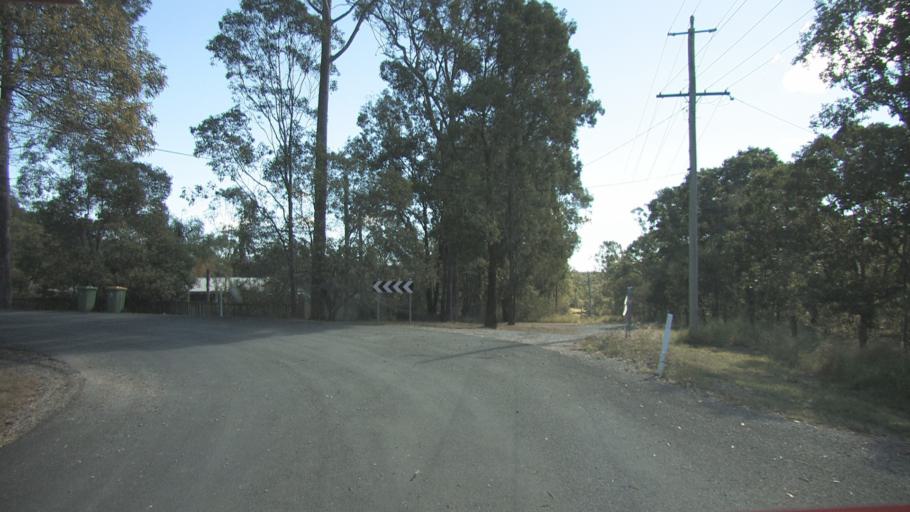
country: AU
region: Queensland
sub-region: Ipswich
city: Springfield Lakes
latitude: -27.7346
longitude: 152.9343
